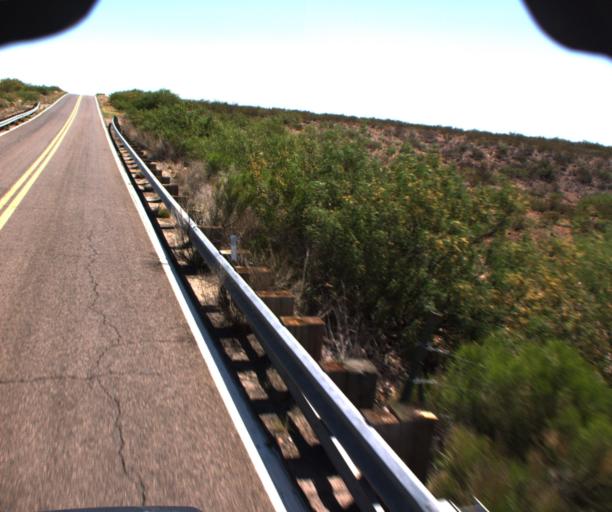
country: US
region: Arizona
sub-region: Cochise County
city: Douglas
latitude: 31.4953
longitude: -109.3347
